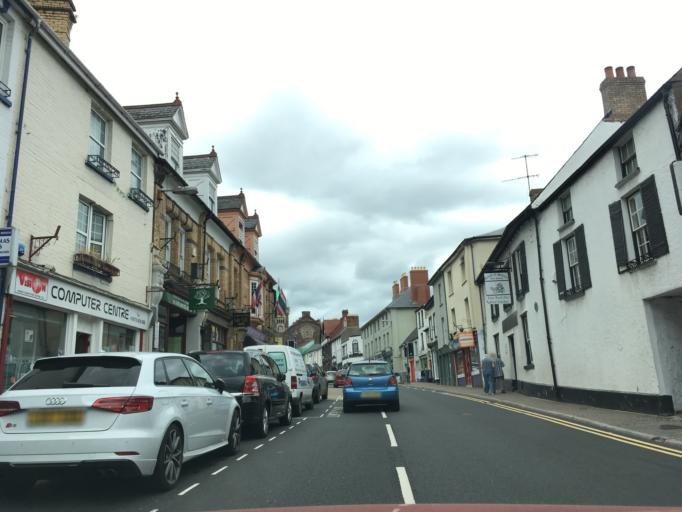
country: GB
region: Wales
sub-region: Monmouthshire
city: Abergavenny
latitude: 51.8204
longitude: -3.0164
